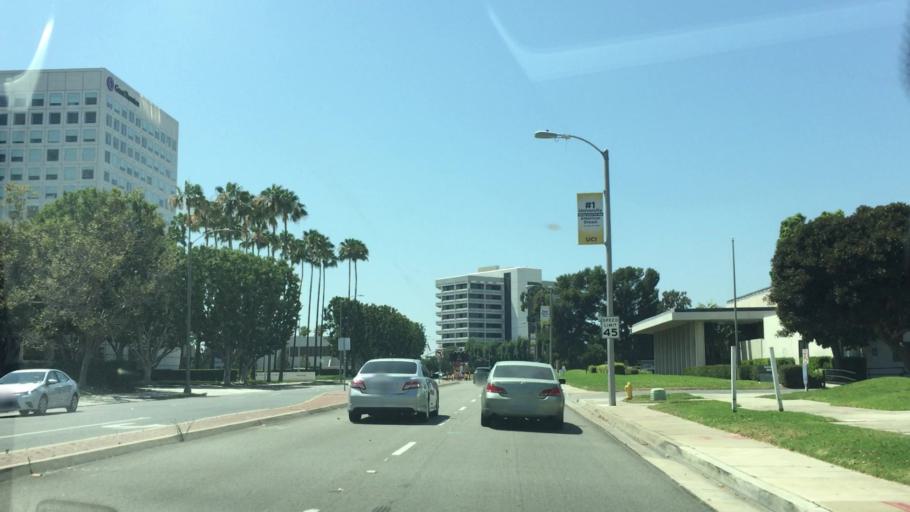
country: US
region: California
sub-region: Orange County
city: Irvine
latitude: 33.6700
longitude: -117.8597
